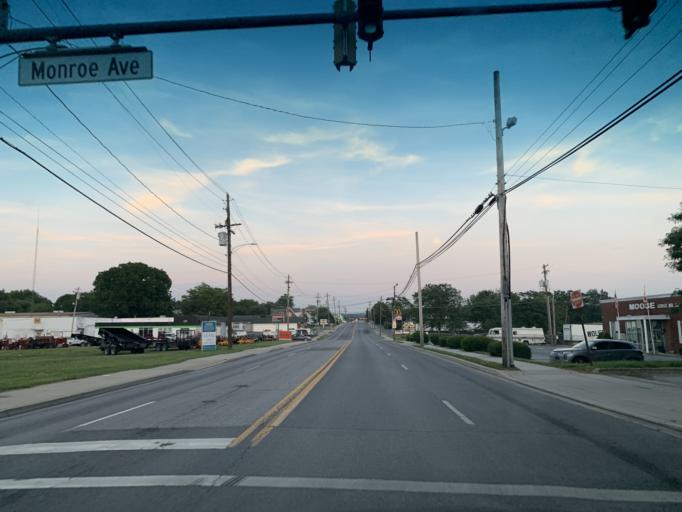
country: US
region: Maryland
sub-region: Frederick County
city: Frederick
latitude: 39.4100
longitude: -77.3932
